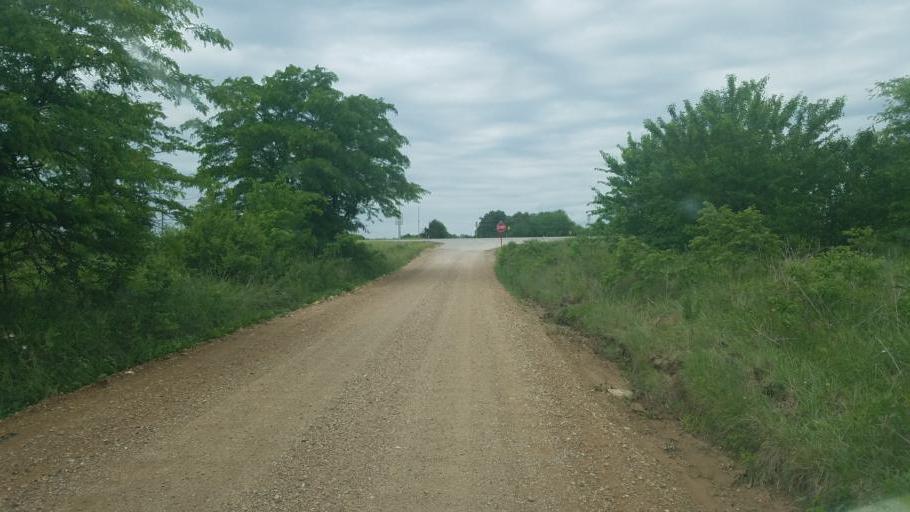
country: US
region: Missouri
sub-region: Moniteau County
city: California
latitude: 38.6341
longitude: -92.6187
